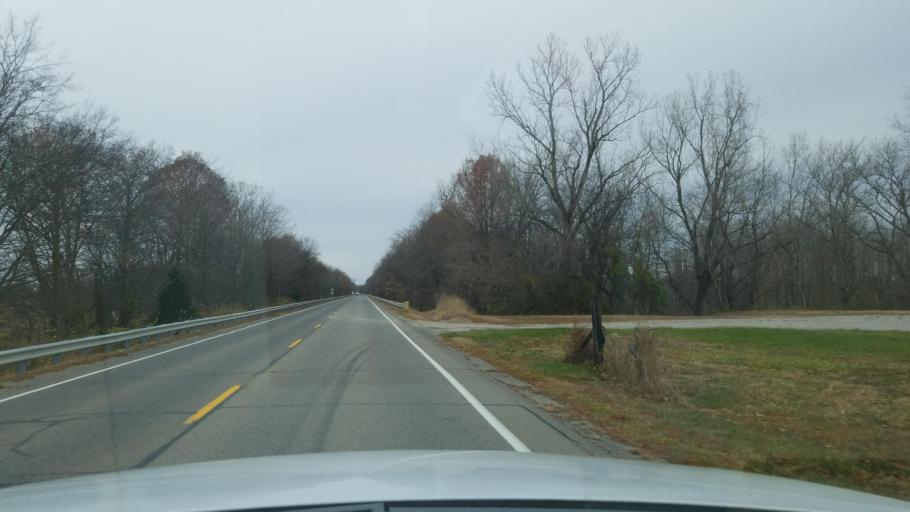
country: US
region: Indiana
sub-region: Posey County
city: Mount Vernon
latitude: 37.9333
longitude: -88.0054
